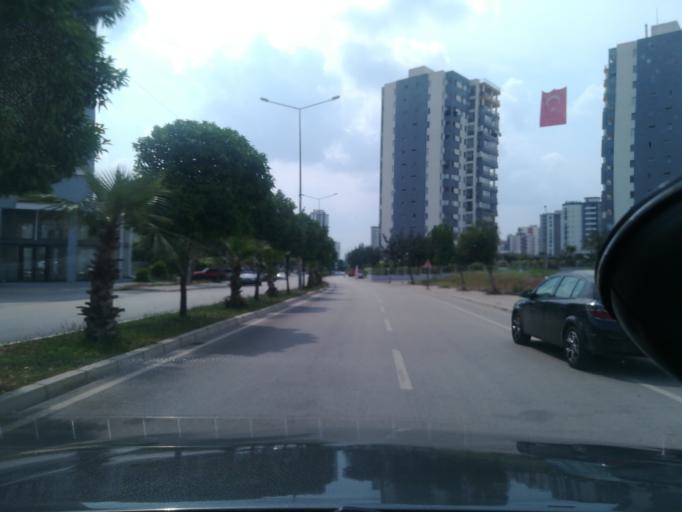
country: TR
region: Adana
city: Seyhan
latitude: 37.0229
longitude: 35.2624
